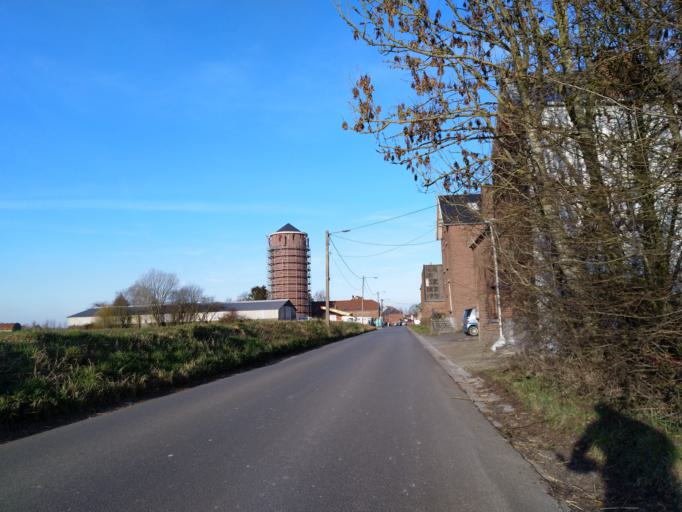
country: FR
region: Nord-Pas-de-Calais
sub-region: Departement du Nord
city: Feignies
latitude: 50.3381
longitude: 3.8995
